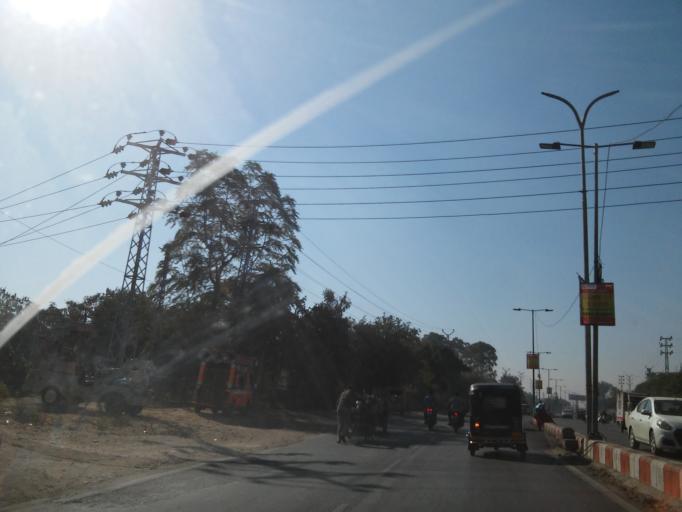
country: IN
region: Rajasthan
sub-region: Udaipur
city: Udaipur
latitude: 24.5632
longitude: 73.6936
